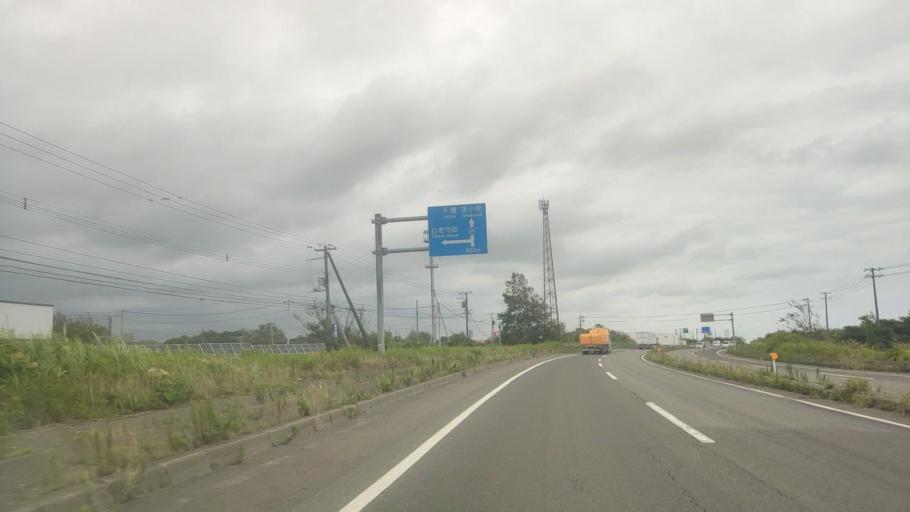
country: JP
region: Hokkaido
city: Shiraoi
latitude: 42.5369
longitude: 141.3325
